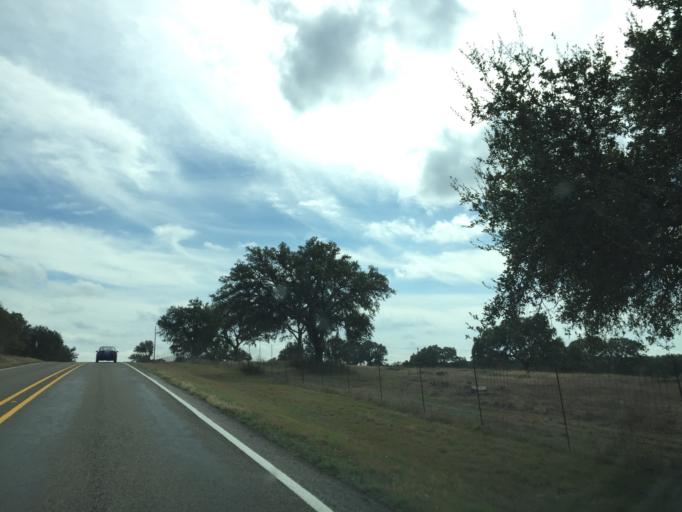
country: US
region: Texas
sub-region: Burnet County
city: Granite Shoals
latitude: 30.5156
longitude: -98.4433
